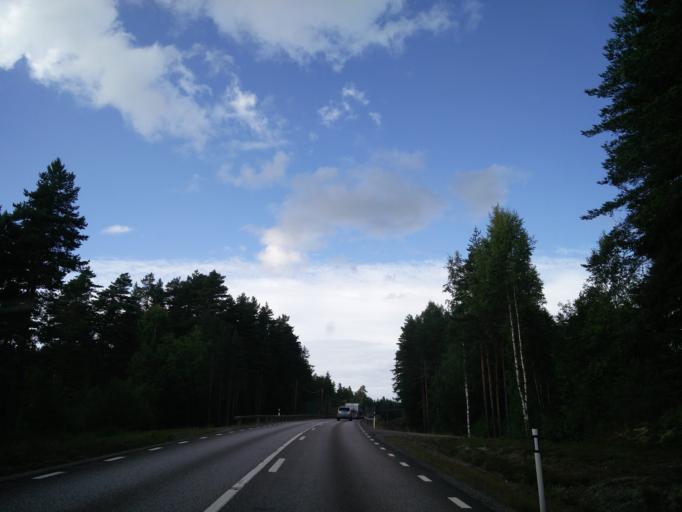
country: SE
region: Vaermland
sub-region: Hagfors Kommun
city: Ekshaerad
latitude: 60.4310
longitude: 13.2562
